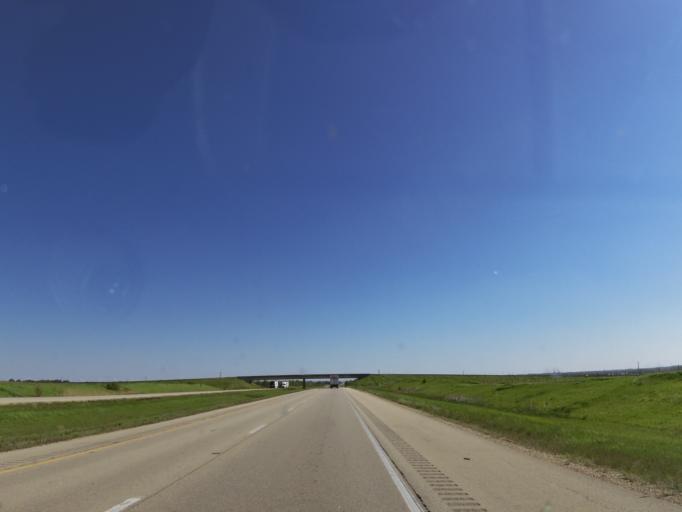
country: US
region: Illinois
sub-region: Ogle County
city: Rochelle
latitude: 41.8212
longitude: -89.0099
